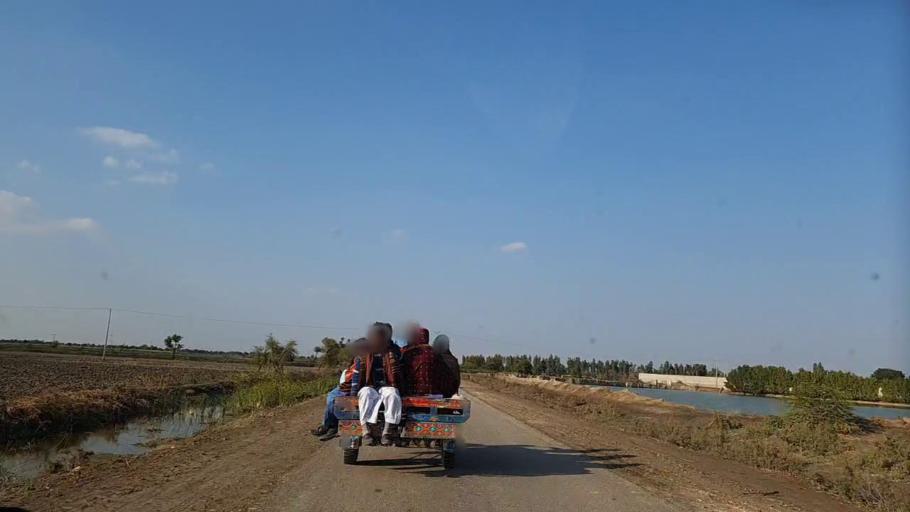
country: PK
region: Sindh
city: Pithoro
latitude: 25.7119
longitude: 69.2206
